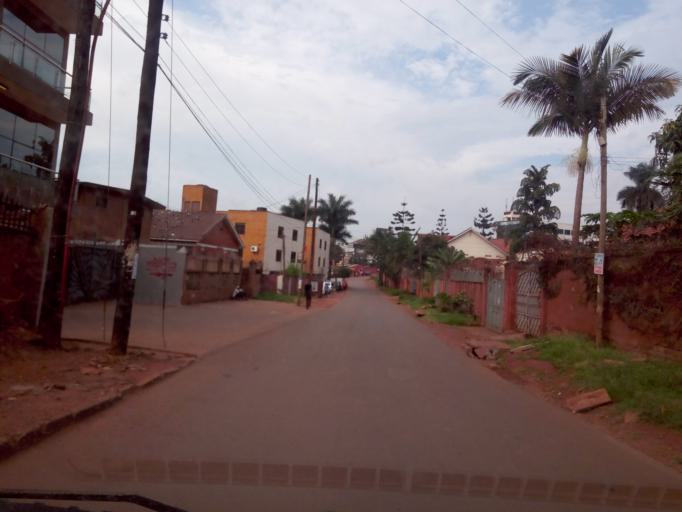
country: UG
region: Central Region
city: Kampala Central Division
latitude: 0.3396
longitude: 32.5855
